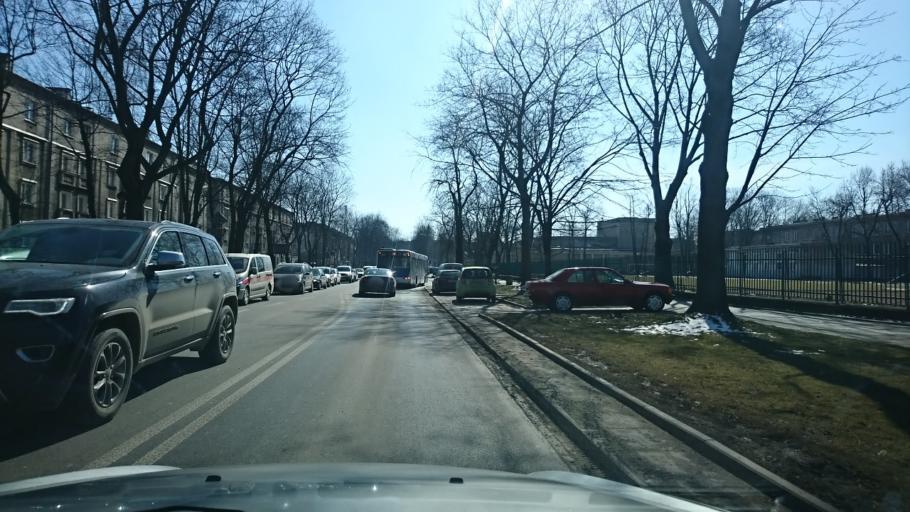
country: PL
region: Lesser Poland Voivodeship
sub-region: Powiat wielicki
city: Kokotow
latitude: 50.0819
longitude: 20.0327
